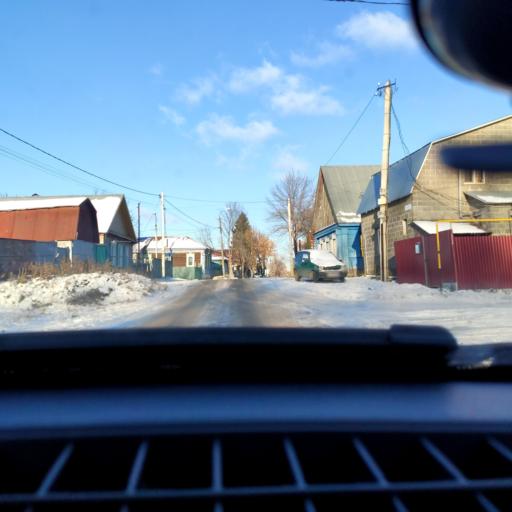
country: RU
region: Bashkortostan
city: Ufa
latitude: 54.7255
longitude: 55.9099
